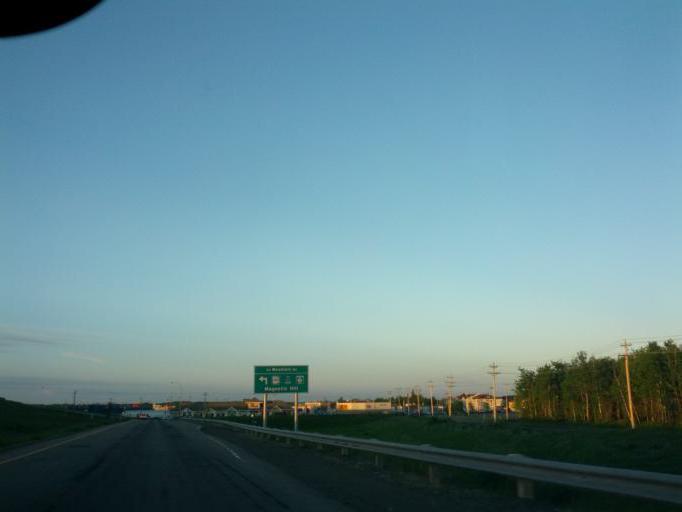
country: CA
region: New Brunswick
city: Moncton
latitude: 46.1111
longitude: -64.8383
